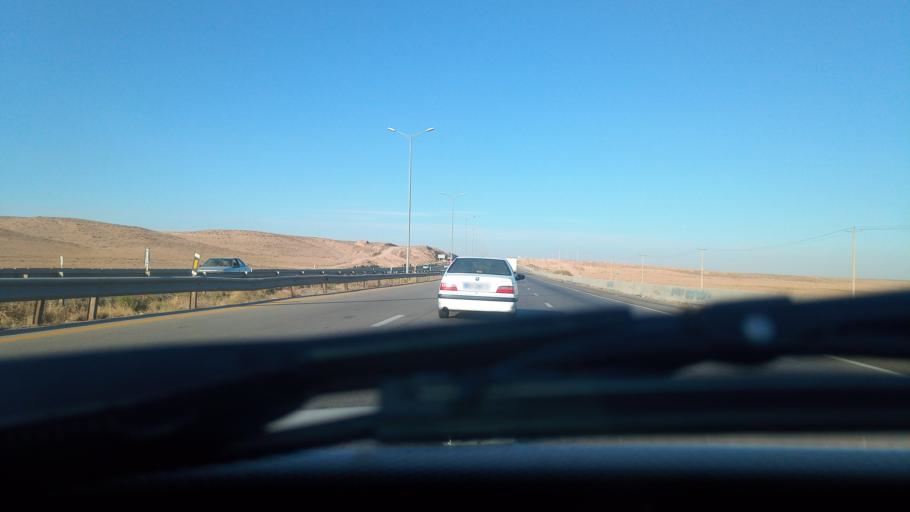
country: IR
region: Razavi Khorasan
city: Mashhad
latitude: 36.0616
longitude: 59.7256
